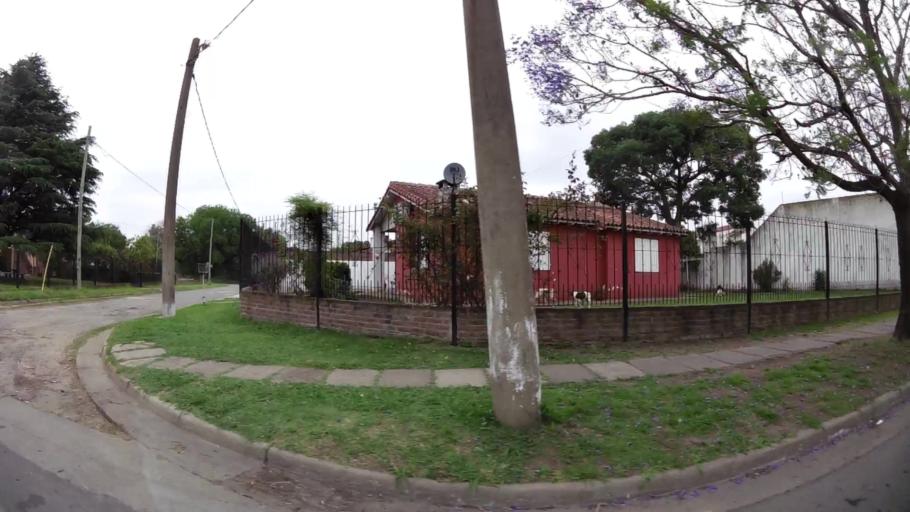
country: AR
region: Buenos Aires
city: San Justo
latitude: -34.7081
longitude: -58.5417
